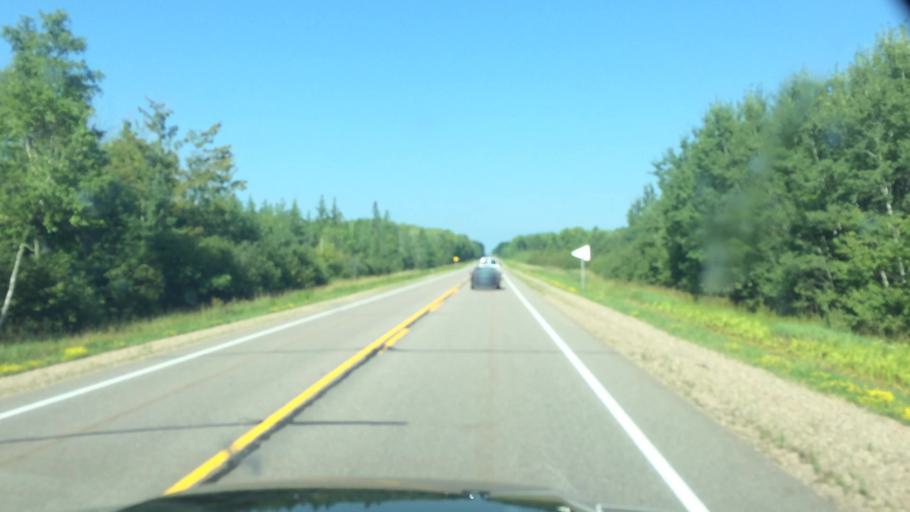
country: US
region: Wisconsin
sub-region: Langlade County
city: Antigo
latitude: 45.1469
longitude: -89.3679
